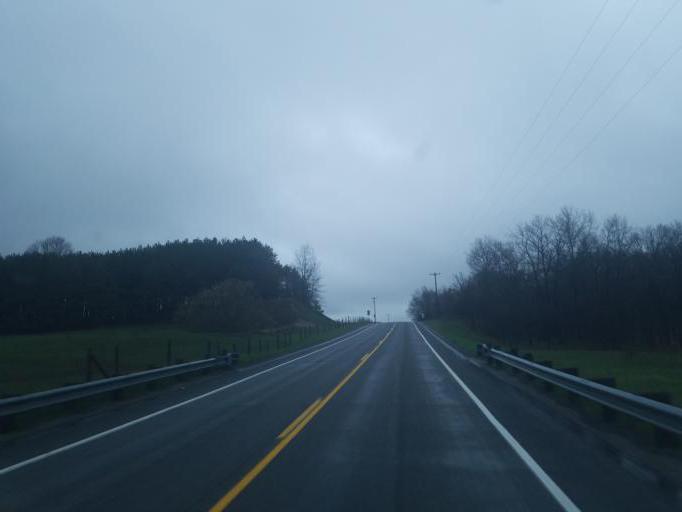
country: US
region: Michigan
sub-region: Montcalm County
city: Edmore
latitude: 43.4351
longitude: -85.0442
